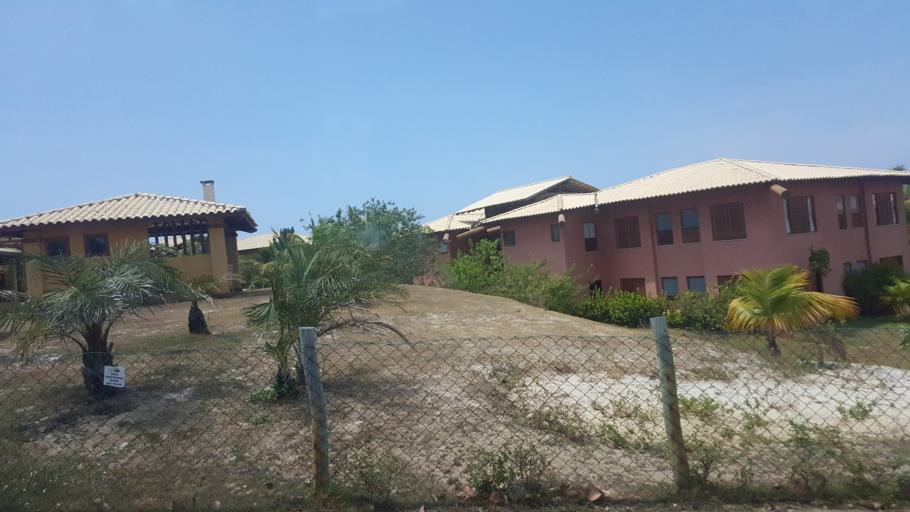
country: BR
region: Bahia
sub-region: Mata De Sao Joao
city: Mata de Sao Joao
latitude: -12.4821
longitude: -37.9609
